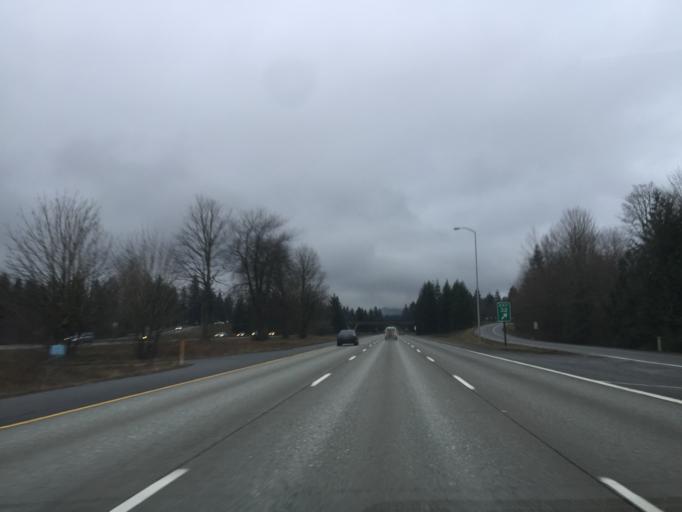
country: US
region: Washington
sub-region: King County
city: Riverbend
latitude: 47.4732
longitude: -121.7633
